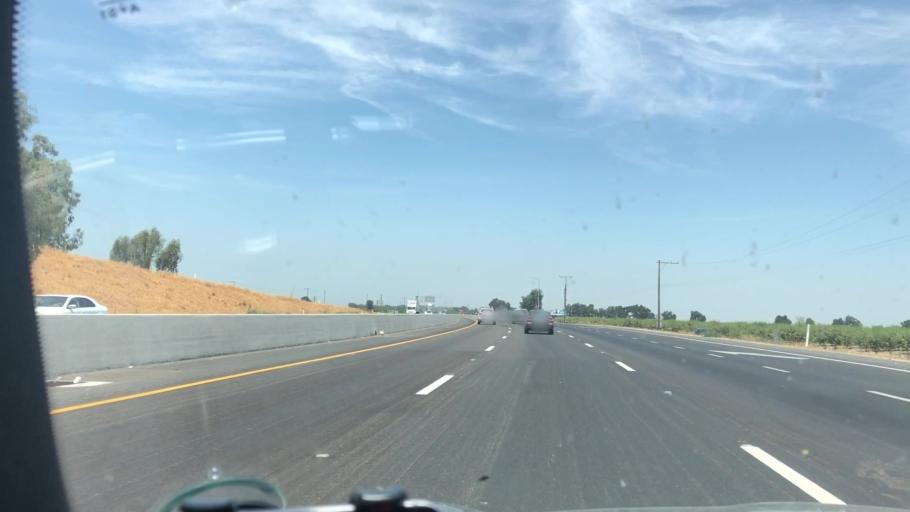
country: US
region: California
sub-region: Tulare County
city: Goshen
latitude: 36.2989
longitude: -119.3850
